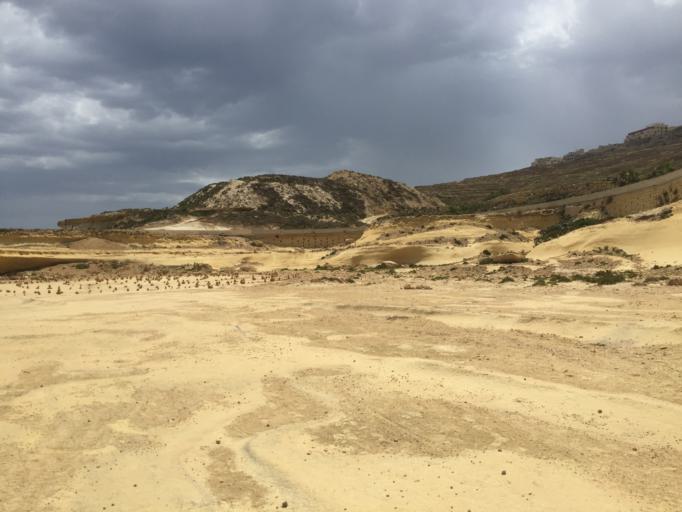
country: MT
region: Iz-Zebbug
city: Zebbug
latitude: 36.0807
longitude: 14.2354
